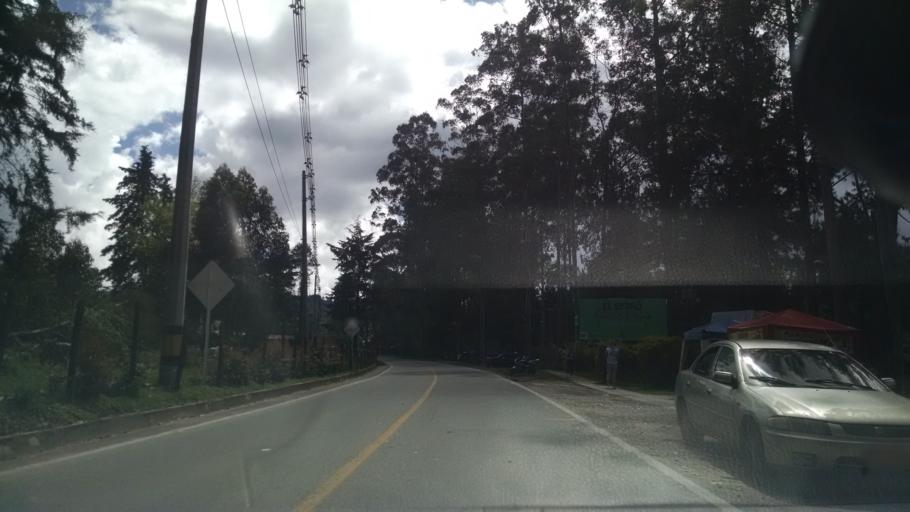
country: CO
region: Antioquia
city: El Retiro
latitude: 6.0706
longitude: -75.4995
